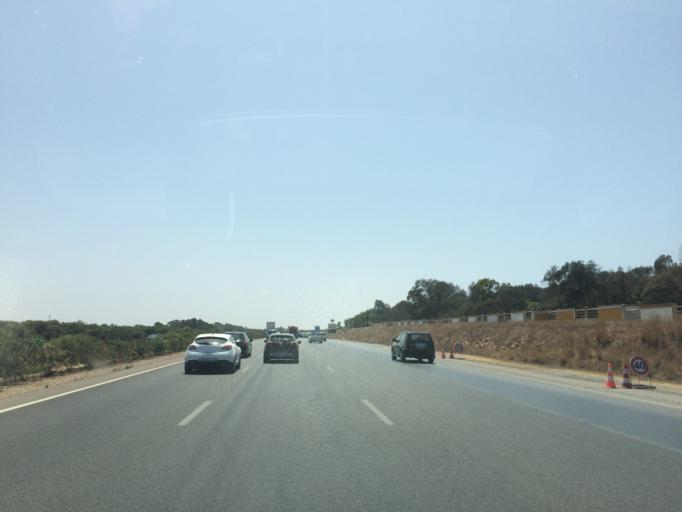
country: MA
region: Rabat-Sale-Zemmour-Zaer
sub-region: Skhirate-Temara
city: Temara
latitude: 33.9466
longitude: -6.9214
